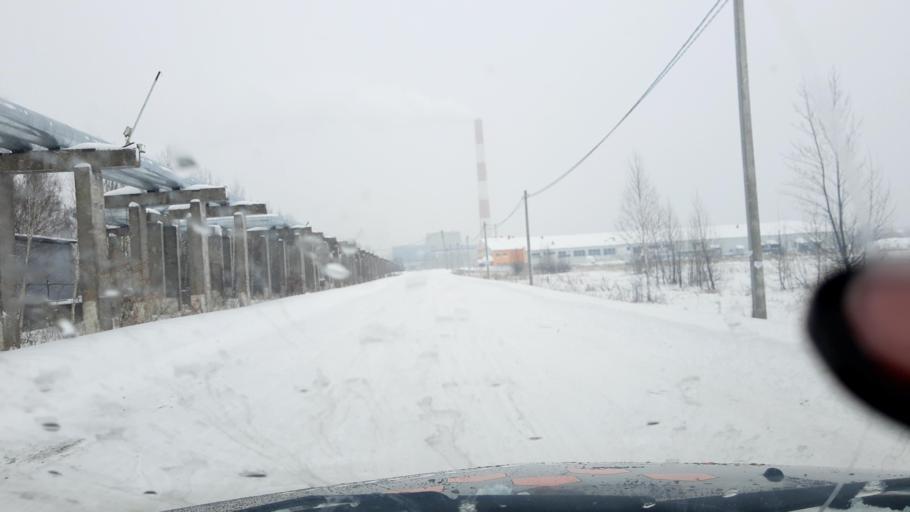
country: RU
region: Bashkortostan
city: Blagoveshchensk
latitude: 55.0296
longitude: 56.0200
